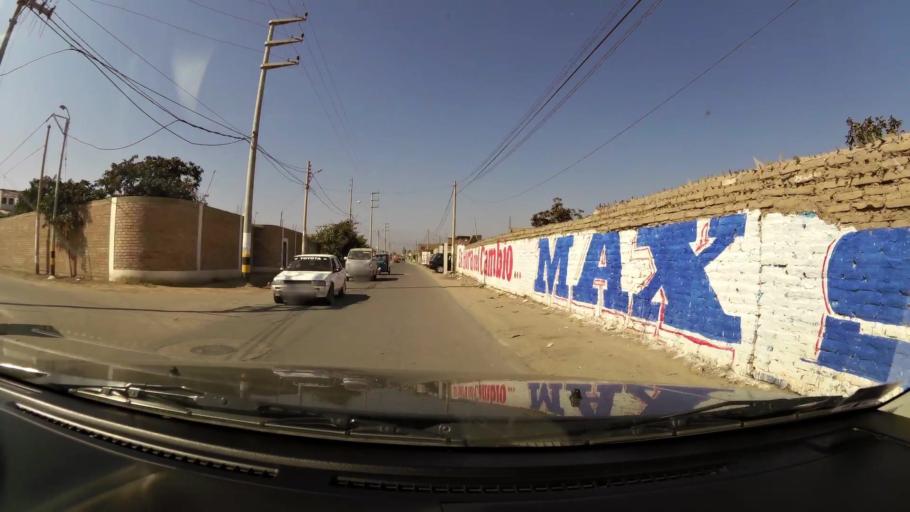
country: PE
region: Ica
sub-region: Provincia de Chincha
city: Sunampe
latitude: -13.4200
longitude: -76.1643
